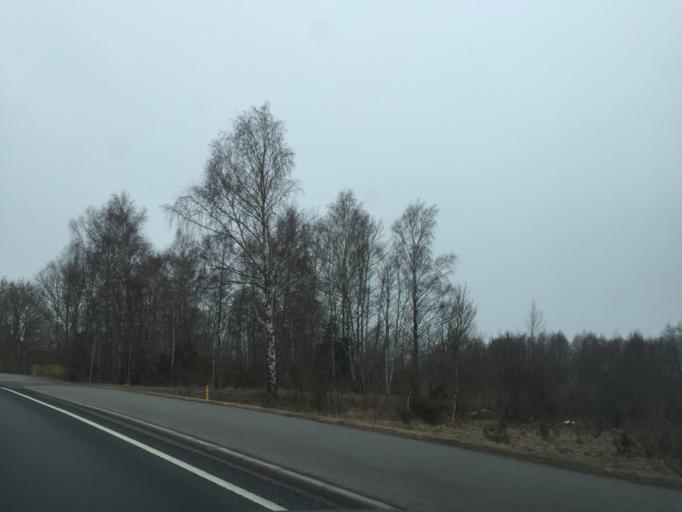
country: EE
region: Laeaene
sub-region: Lihula vald
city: Lihula
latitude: 58.5856
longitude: 23.5268
